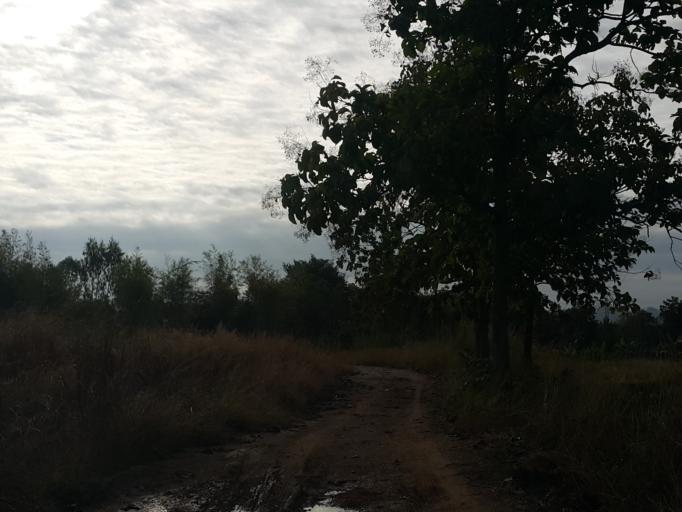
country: TH
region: Lampang
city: Mae Mo
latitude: 18.2522
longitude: 99.5956
